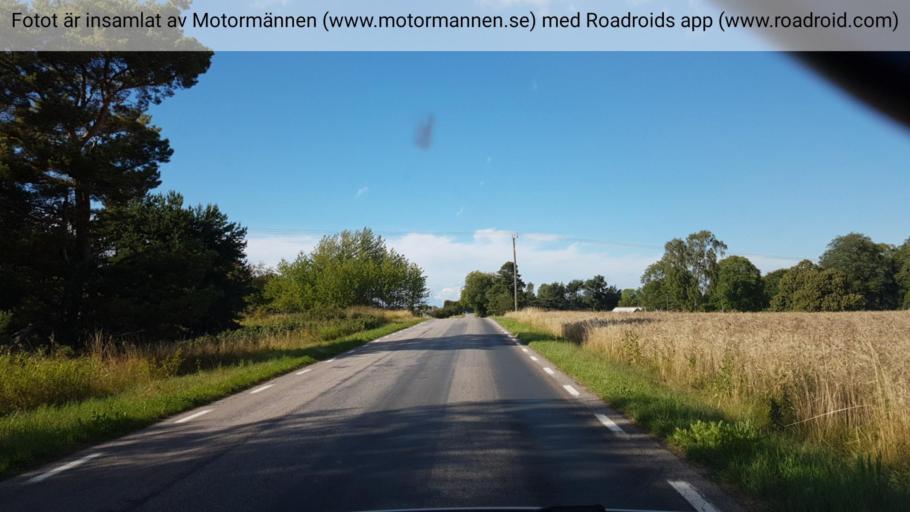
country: SE
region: Vaestra Goetaland
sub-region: Gotene Kommun
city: Kallby
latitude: 58.4981
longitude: 13.3134
